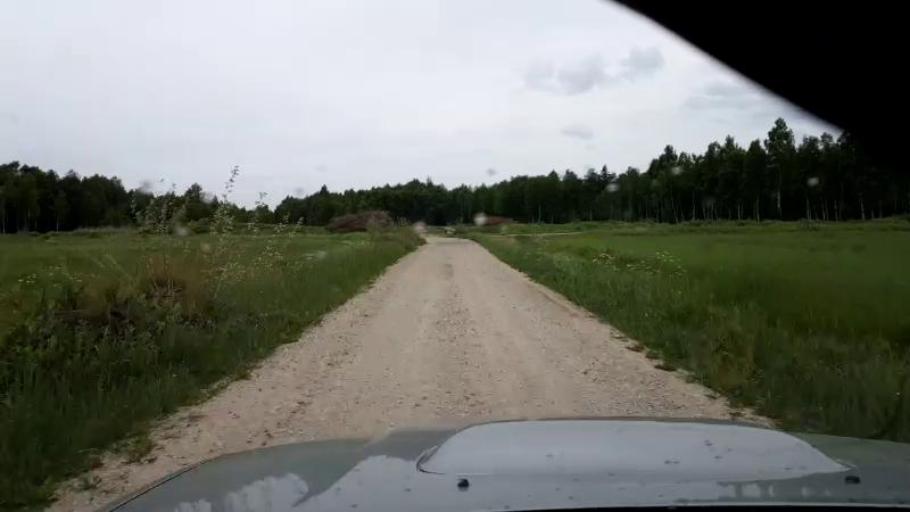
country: EE
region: Paernumaa
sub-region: Halinga vald
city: Parnu-Jaagupi
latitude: 58.5429
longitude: 24.5978
